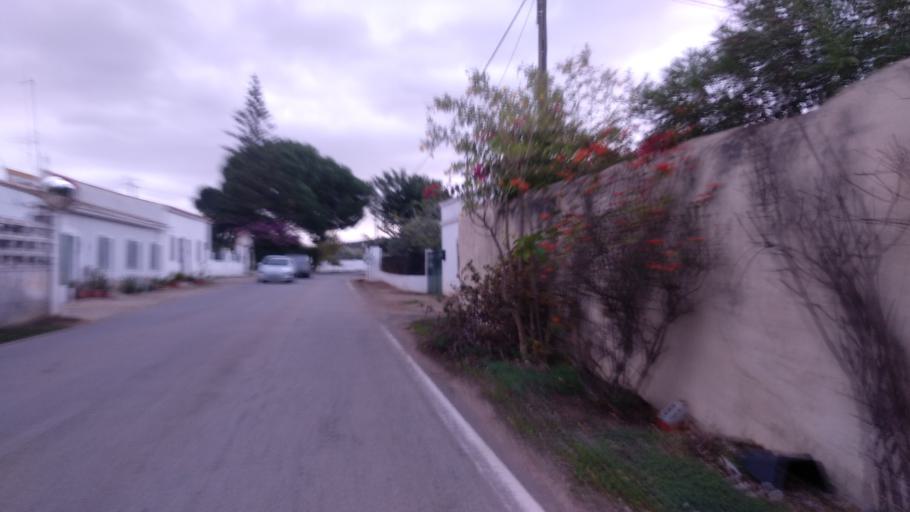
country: PT
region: Faro
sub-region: Sao Bras de Alportel
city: Sao Bras de Alportel
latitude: 37.1727
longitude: -7.9087
